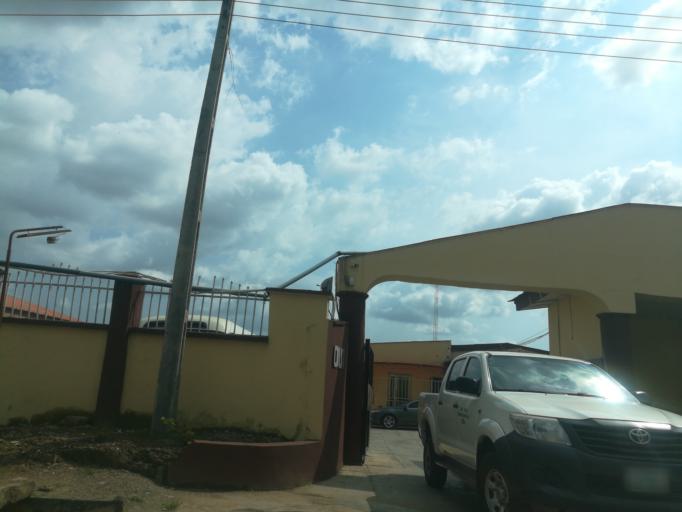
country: NG
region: Oyo
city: Ibadan
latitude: 7.3641
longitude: 3.8500
